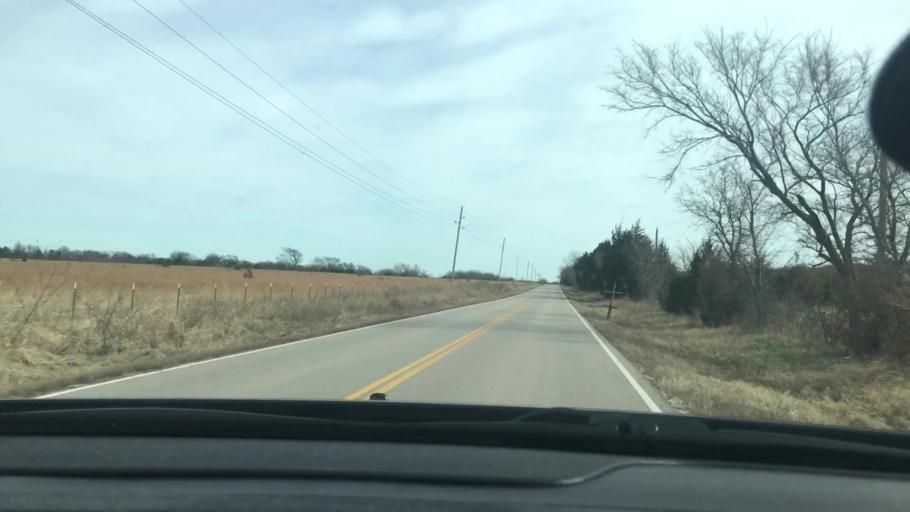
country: US
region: Oklahoma
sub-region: Murray County
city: Sulphur
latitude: 34.4048
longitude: -96.8543
